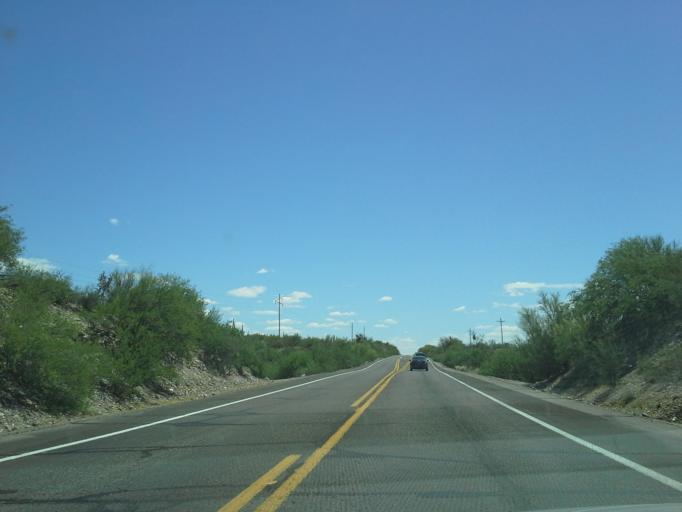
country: US
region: Arizona
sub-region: Pinal County
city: Mammoth
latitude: 32.7934
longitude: -110.6746
